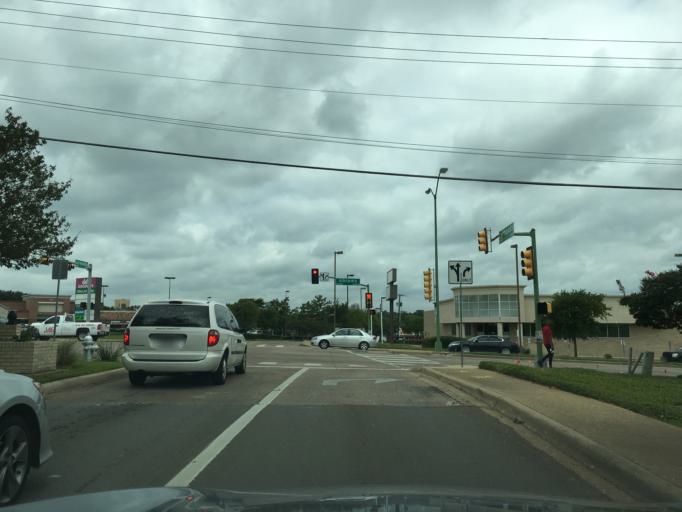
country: US
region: Texas
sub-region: Dallas County
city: Highland Park
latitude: 32.8626
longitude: -96.7441
